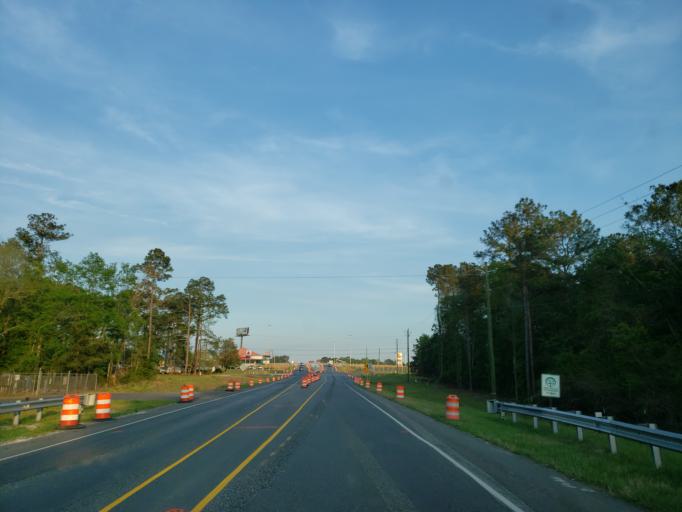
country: US
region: Georgia
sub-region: Lowndes County
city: Hahira
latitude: 30.9937
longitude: -83.3931
